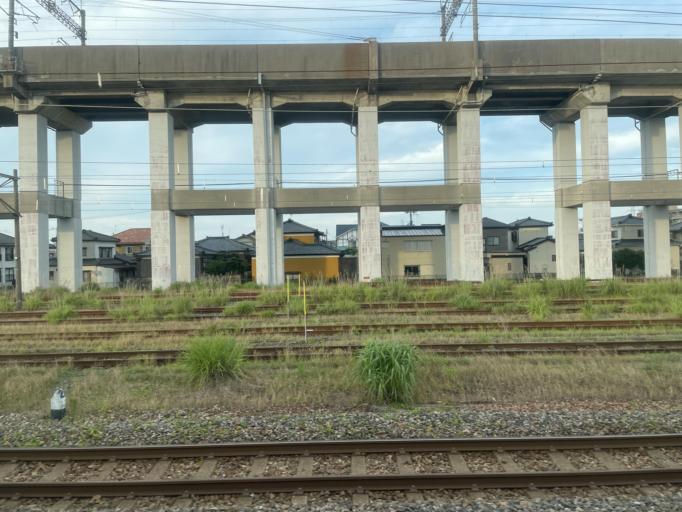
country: JP
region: Niigata
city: Kameda-honcho
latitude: 37.9096
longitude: 139.0805
